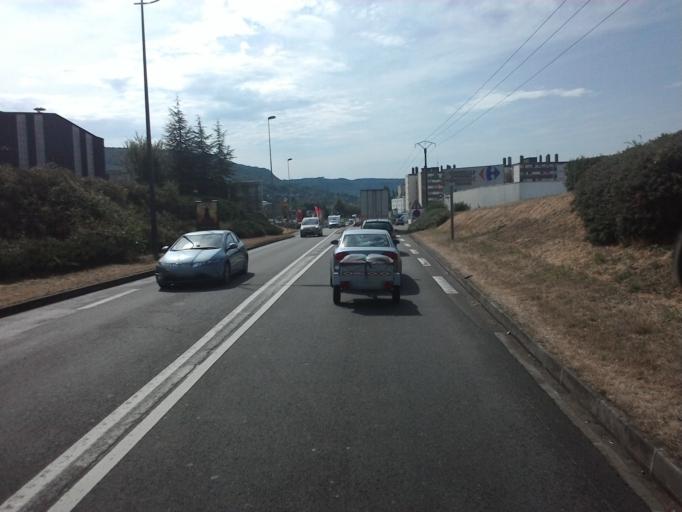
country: FR
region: Franche-Comte
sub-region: Departement du Jura
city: Perrigny
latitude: 46.6808
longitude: 5.5711
